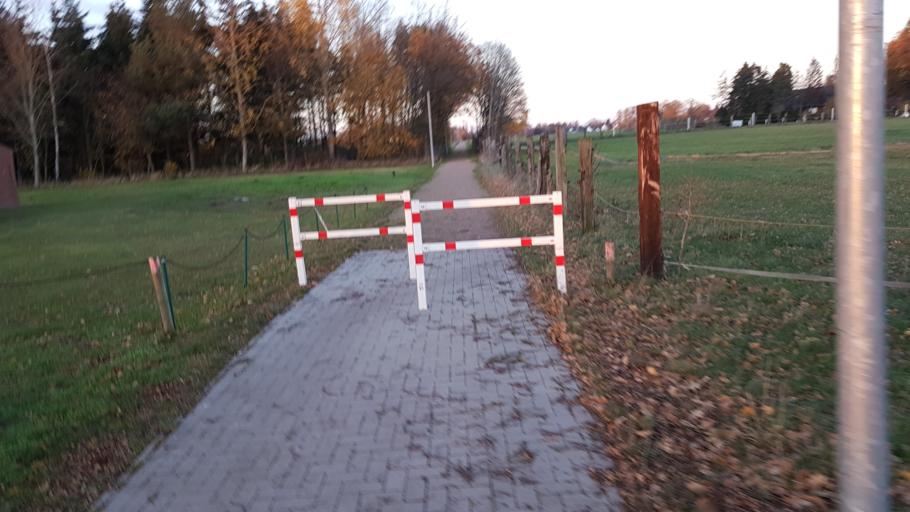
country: DE
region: North Rhine-Westphalia
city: Rahden
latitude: 52.4324
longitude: 8.6302
